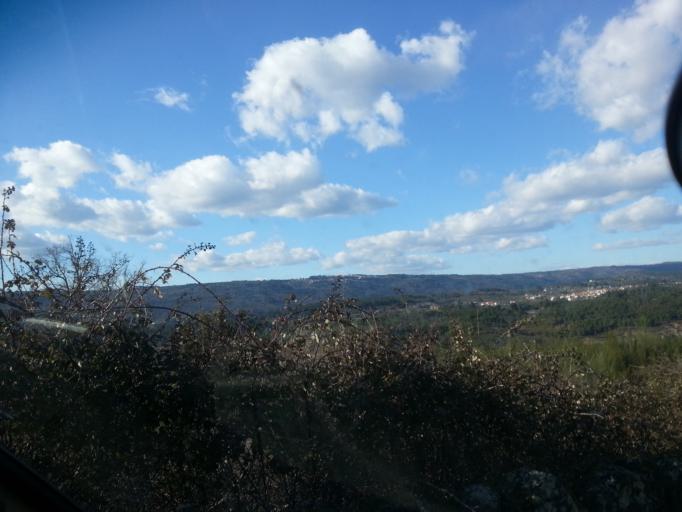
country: PT
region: Guarda
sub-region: Fornos de Algodres
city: Fornos de Algodres
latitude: 40.6116
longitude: -7.5006
